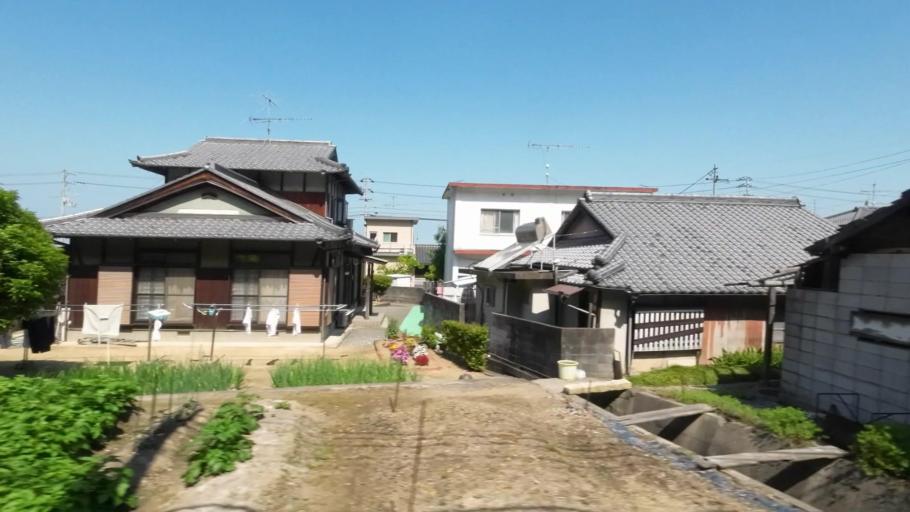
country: JP
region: Ehime
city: Kawanoecho
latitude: 34.0355
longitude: 133.5943
